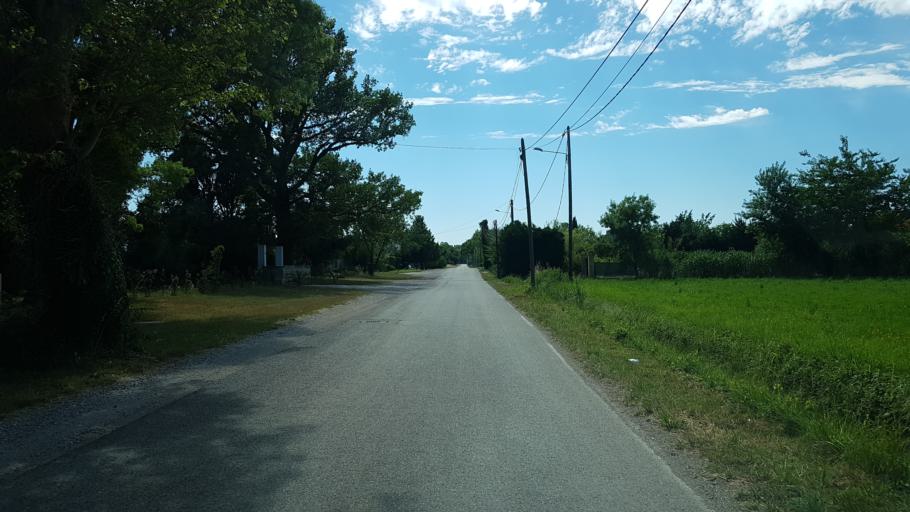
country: FR
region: Provence-Alpes-Cote d'Azur
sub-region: Departement des Bouches-du-Rhone
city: Saint-Martin-de-Crau
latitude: 43.6601
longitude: 4.7486
